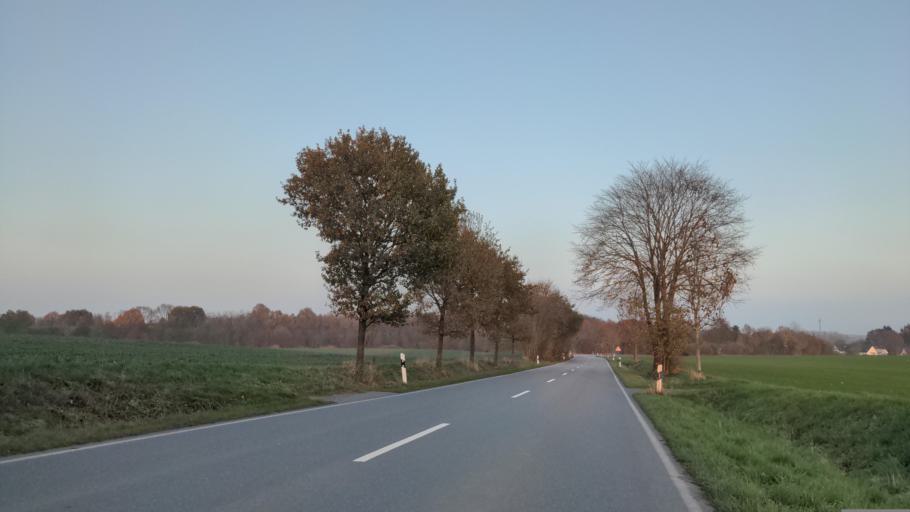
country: DE
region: Schleswig-Holstein
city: Eutin
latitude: 54.1187
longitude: 10.5597
